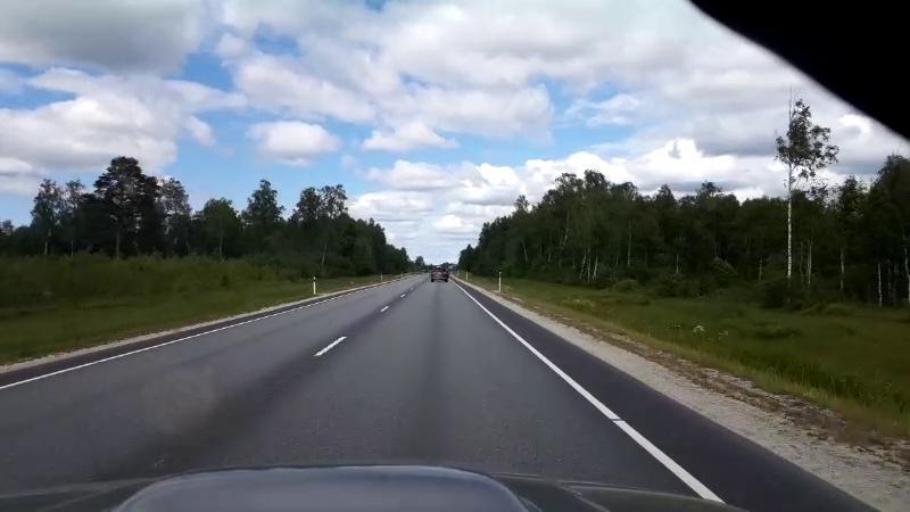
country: EE
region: Harju
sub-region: Nissi vald
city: Riisipere
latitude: 59.0691
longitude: 24.4514
